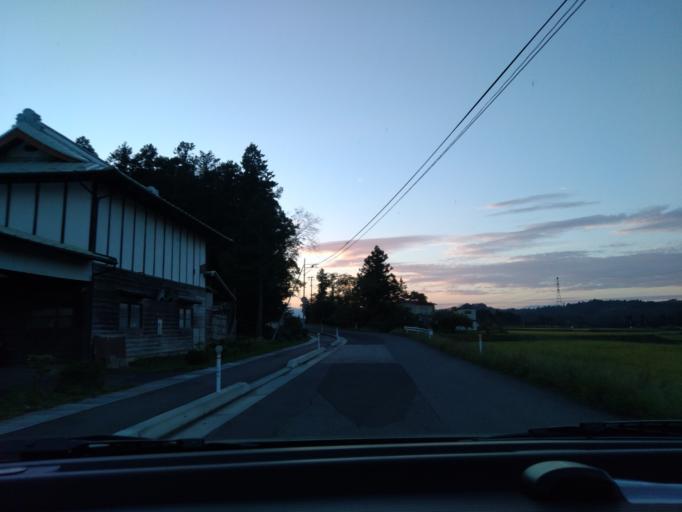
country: JP
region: Iwate
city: Ichinoseki
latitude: 38.8529
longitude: 141.1555
